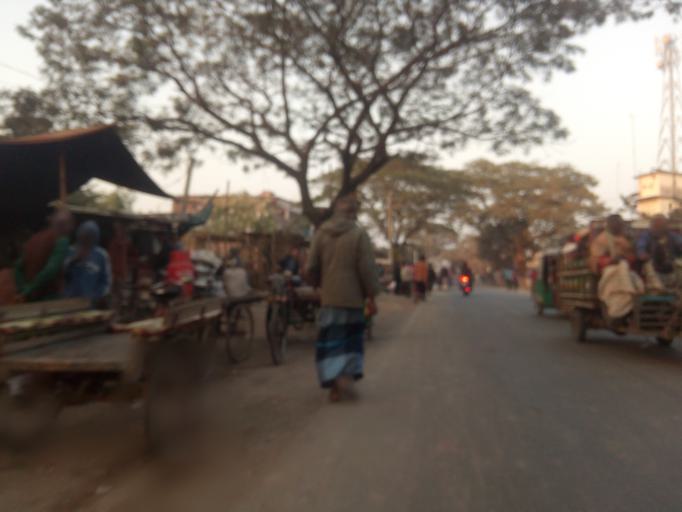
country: BD
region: Rajshahi
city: Bogra
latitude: 24.6452
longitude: 89.2546
